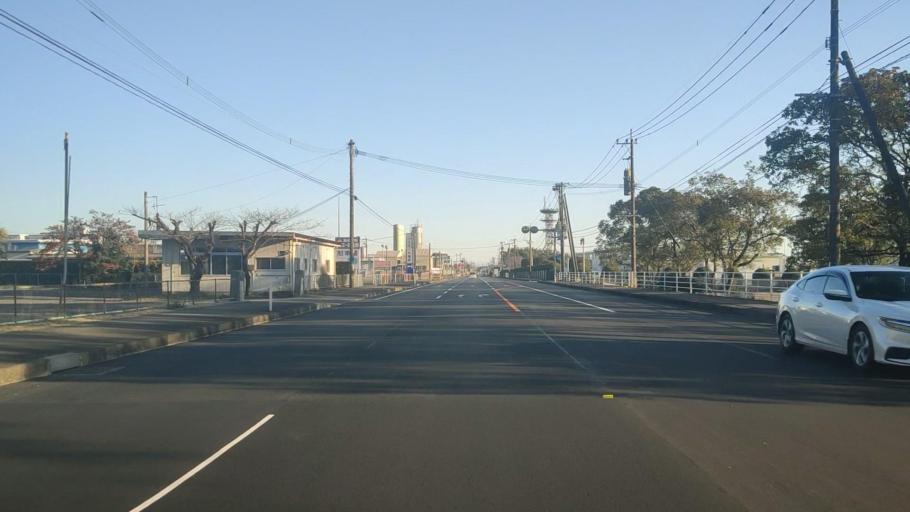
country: JP
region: Miyazaki
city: Takanabe
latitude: 32.2218
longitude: 131.5422
